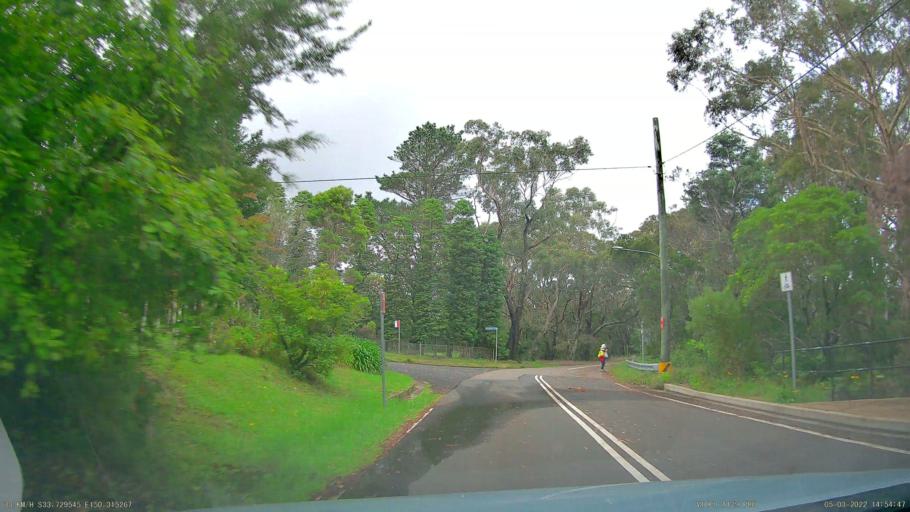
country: AU
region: New South Wales
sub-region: Blue Mountains Municipality
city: Katoomba
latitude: -33.7294
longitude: 150.3154
